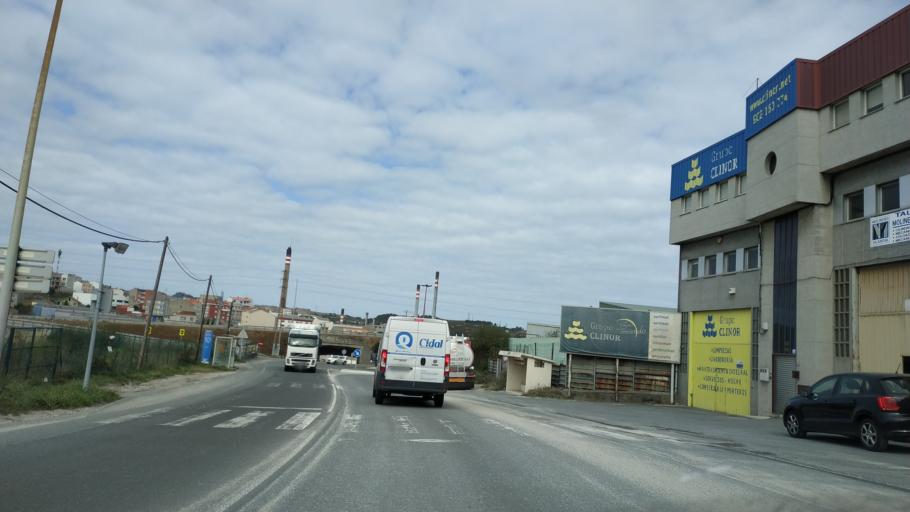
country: ES
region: Galicia
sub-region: Provincia da Coruna
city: A Coruna
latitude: 43.3410
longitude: -8.4442
